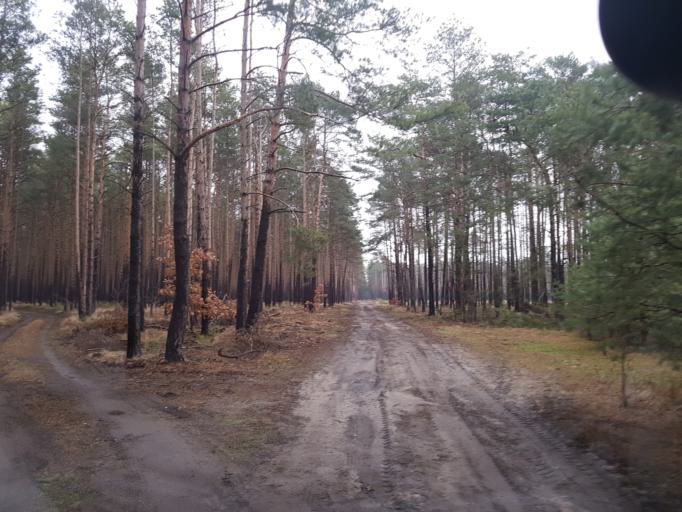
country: DE
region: Brandenburg
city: Finsterwalde
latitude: 51.5711
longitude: 13.6853
